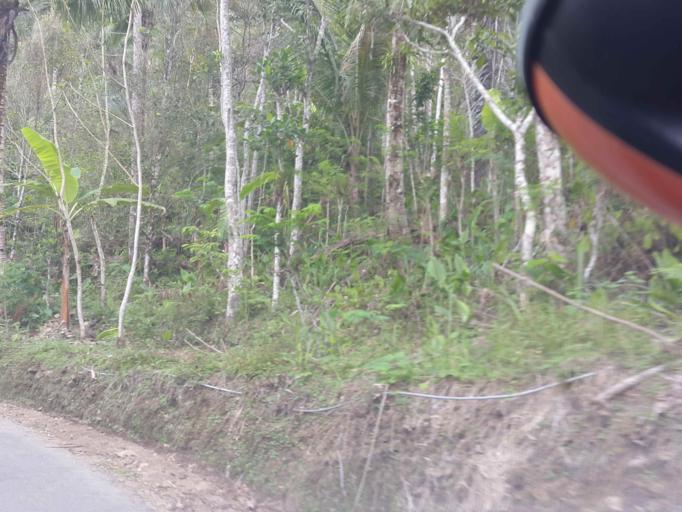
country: ID
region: East Java
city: Ploso
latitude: -8.0406
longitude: 111.1336
